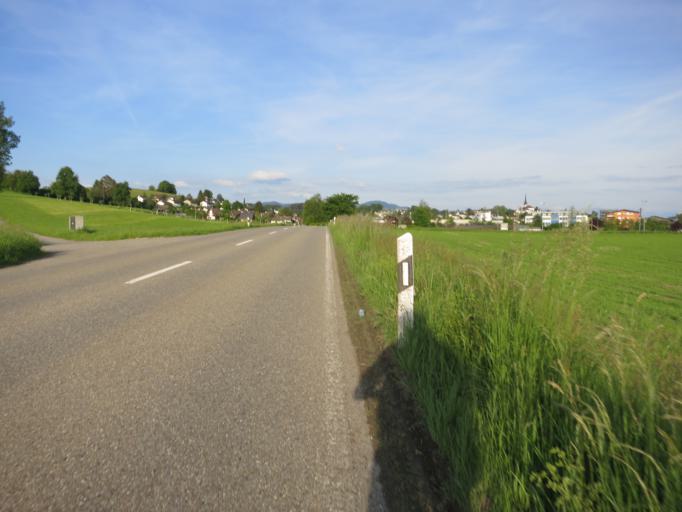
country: CH
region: Zurich
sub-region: Bezirk Hinwil
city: Gossau
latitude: 47.3062
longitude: 8.7448
